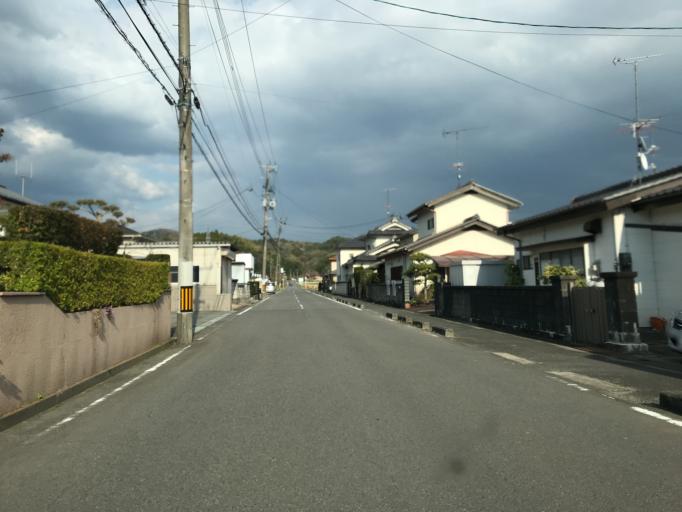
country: JP
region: Fukushima
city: Iwaki
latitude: 37.0880
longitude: 140.8782
